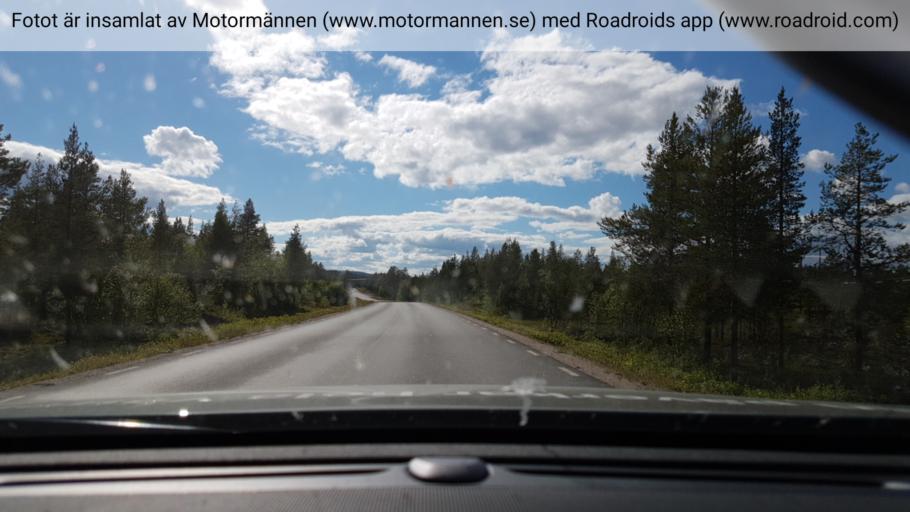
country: SE
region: Norrbotten
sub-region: Arjeplogs Kommun
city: Arjeplog
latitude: 66.0697
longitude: 17.6331
